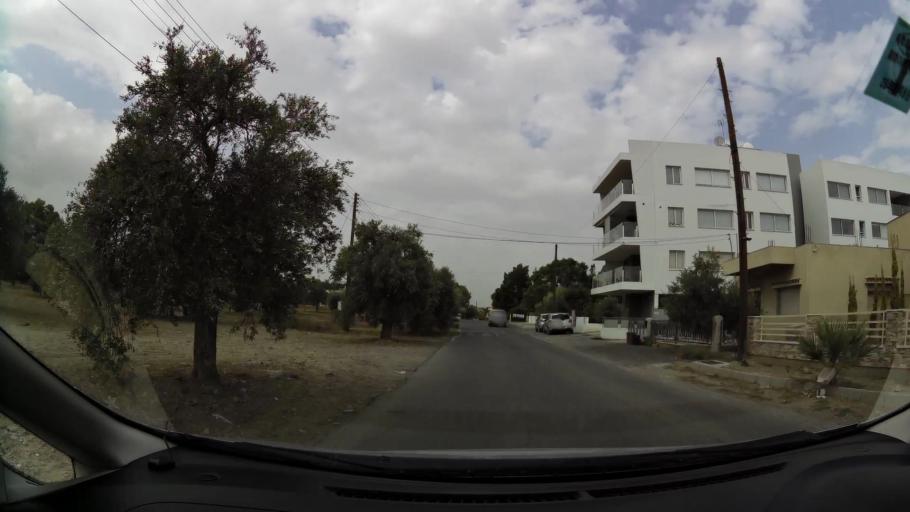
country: CY
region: Lefkosia
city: Geri
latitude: 35.1064
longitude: 33.3732
